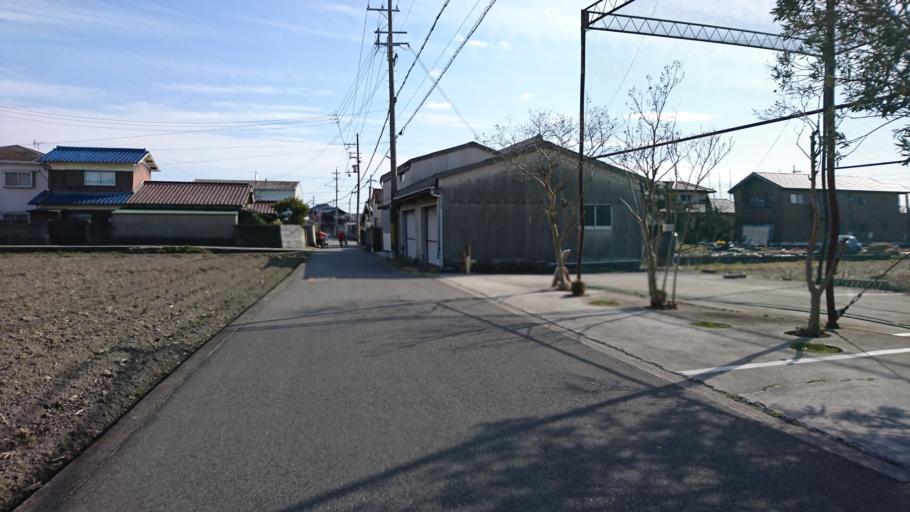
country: JP
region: Hyogo
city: Kakogawacho-honmachi
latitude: 34.7826
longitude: 134.8354
